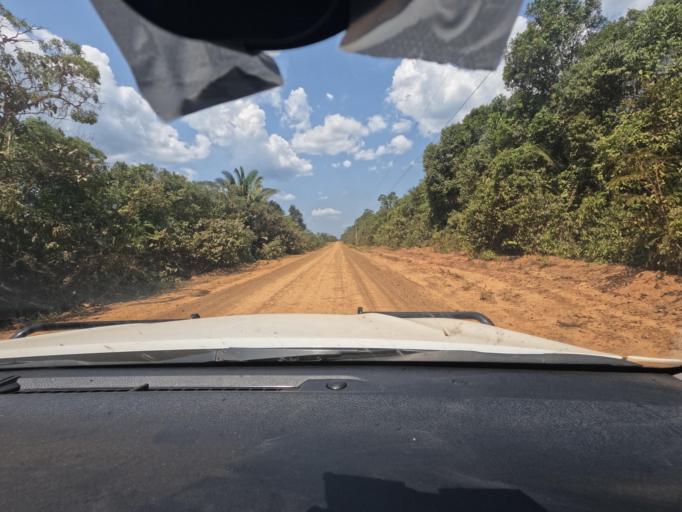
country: BR
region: Amazonas
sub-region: Humaita
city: Humaita
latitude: -7.4998
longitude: -63.6252
